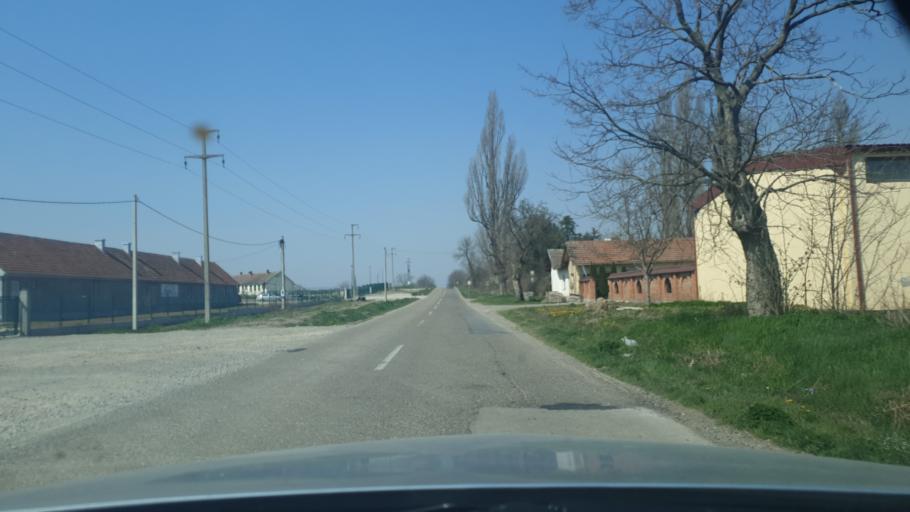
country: RS
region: Autonomna Pokrajina Vojvodina
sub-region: Sremski Okrug
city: Ruma
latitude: 45.0097
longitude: 19.7859
